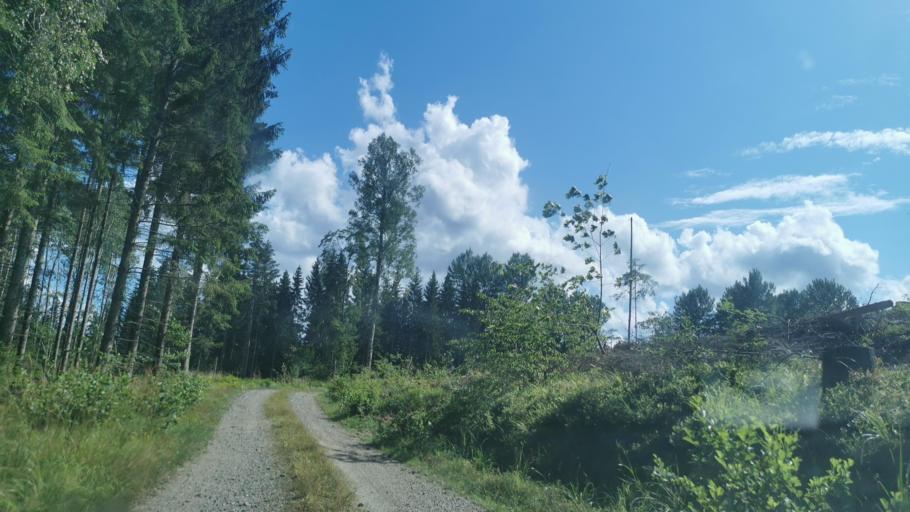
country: SE
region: OEstergoetland
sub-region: Finspangs Kommun
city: Finspang
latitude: 58.7996
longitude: 15.8045
